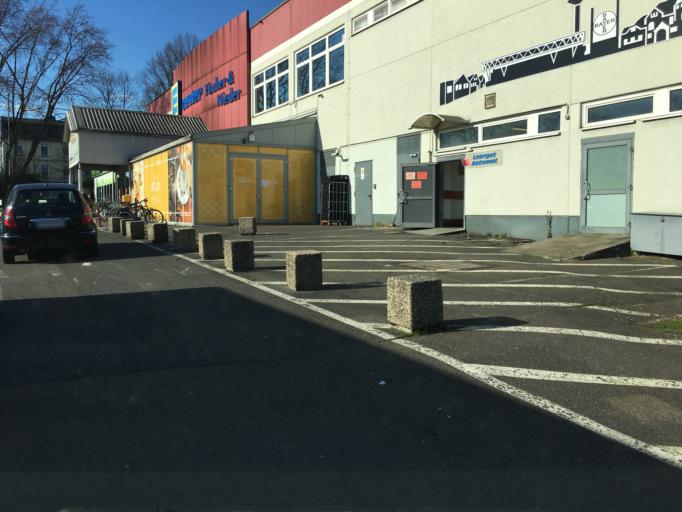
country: DE
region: North Rhine-Westphalia
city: Opladen
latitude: 51.0534
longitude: 7.0009
